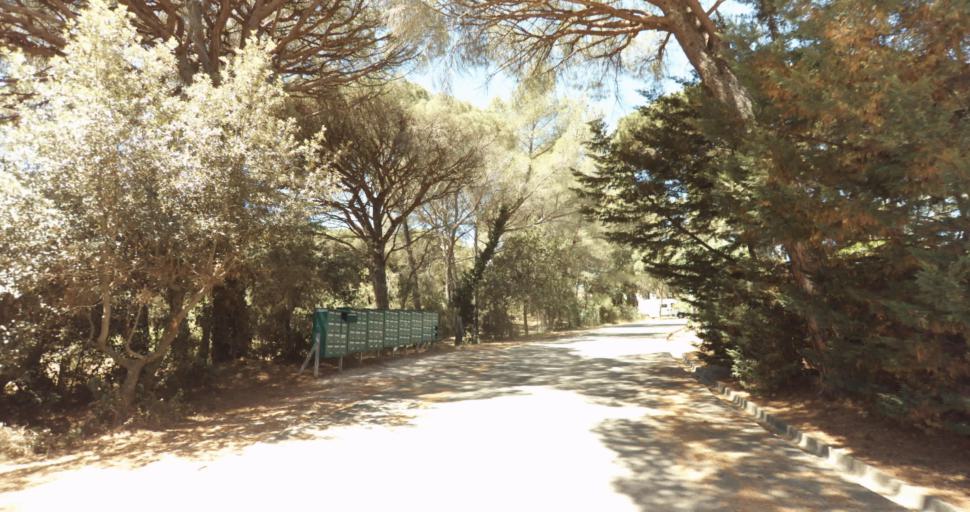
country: FR
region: Provence-Alpes-Cote d'Azur
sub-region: Departement du Var
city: Gassin
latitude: 43.2574
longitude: 6.5689
